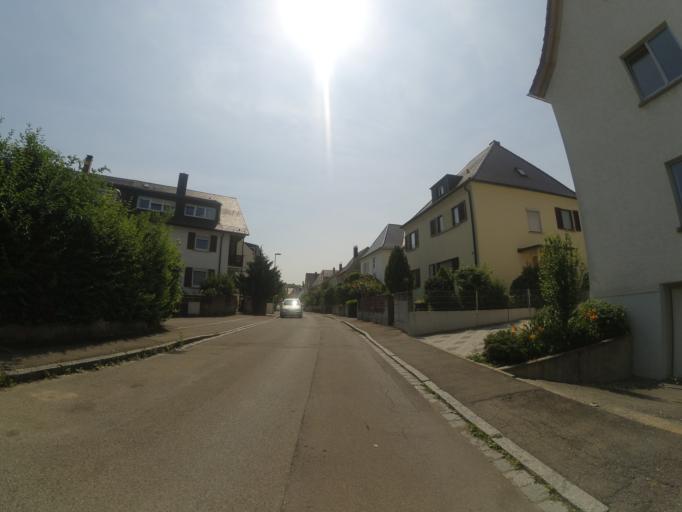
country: DE
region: Baden-Wuerttemberg
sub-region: Tuebingen Region
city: Ulm
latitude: 48.3891
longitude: 9.9747
